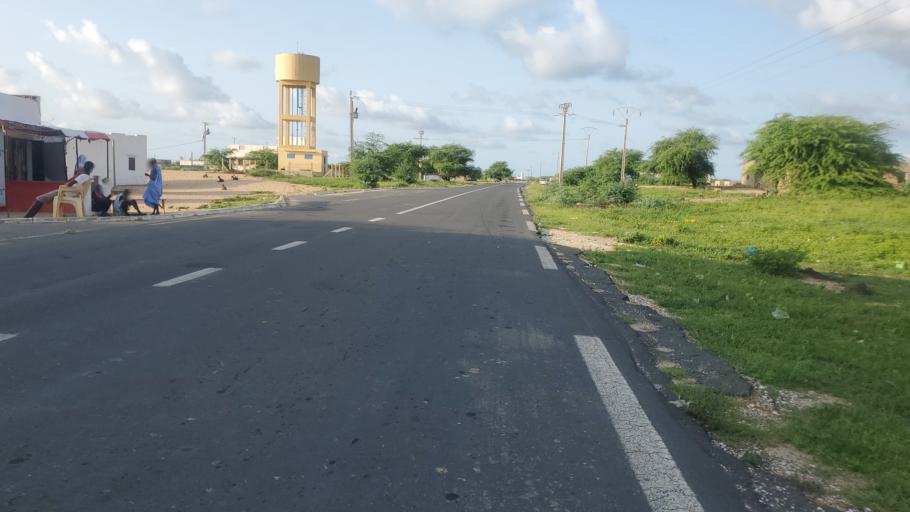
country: SN
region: Saint-Louis
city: Saint-Louis
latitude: 16.1355
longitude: -16.4114
